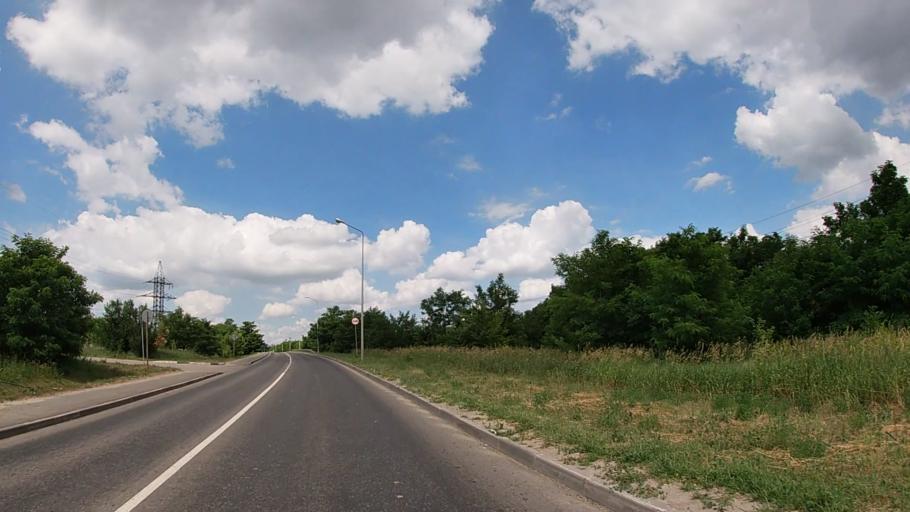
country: RU
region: Belgorod
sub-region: Belgorodskiy Rayon
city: Belgorod
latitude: 50.5936
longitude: 36.5589
